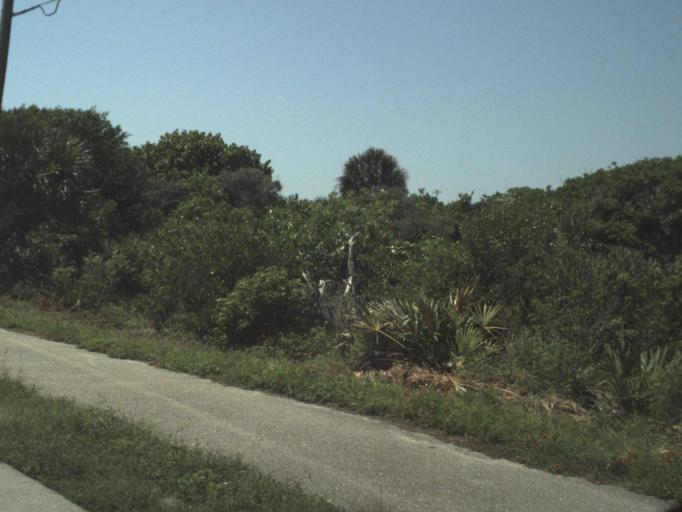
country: US
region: Florida
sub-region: Brevard County
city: Malabar
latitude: 28.0007
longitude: -80.5257
